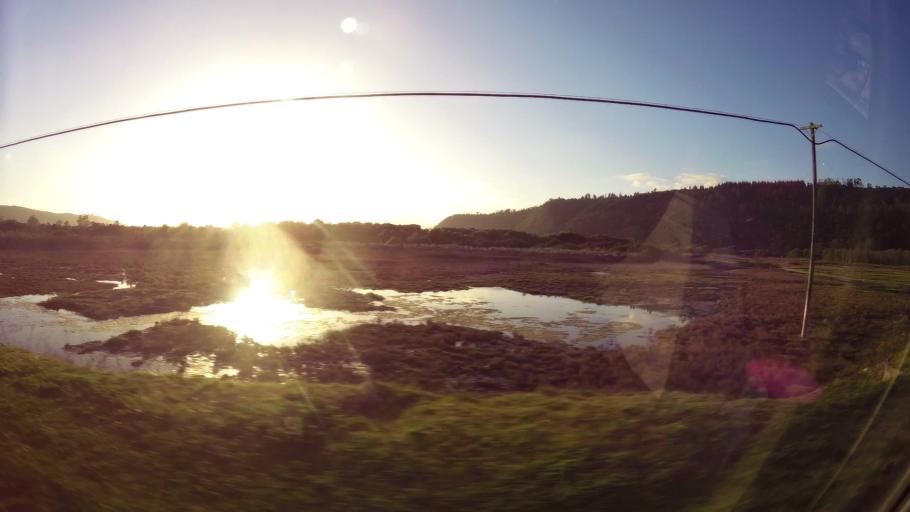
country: ZA
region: Western Cape
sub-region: Eden District Municipality
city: Knysna
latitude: -34.0136
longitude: 22.7889
